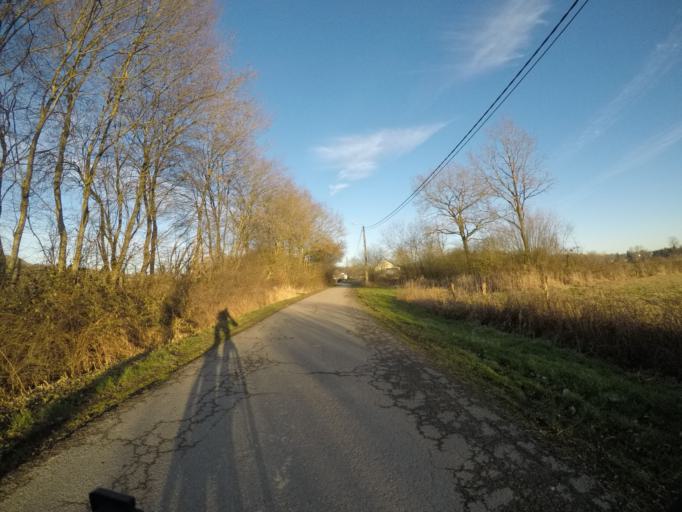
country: BE
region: Wallonia
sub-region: Province du Luxembourg
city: Habay-la-Vieille
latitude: 49.7246
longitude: 5.6084
